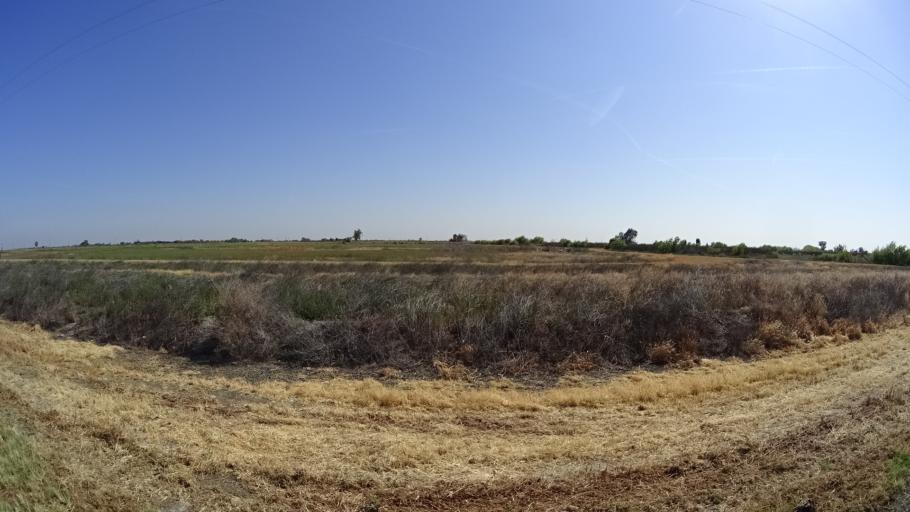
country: US
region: California
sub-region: Fresno County
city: Riverdale
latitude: 36.3735
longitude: -119.9254
